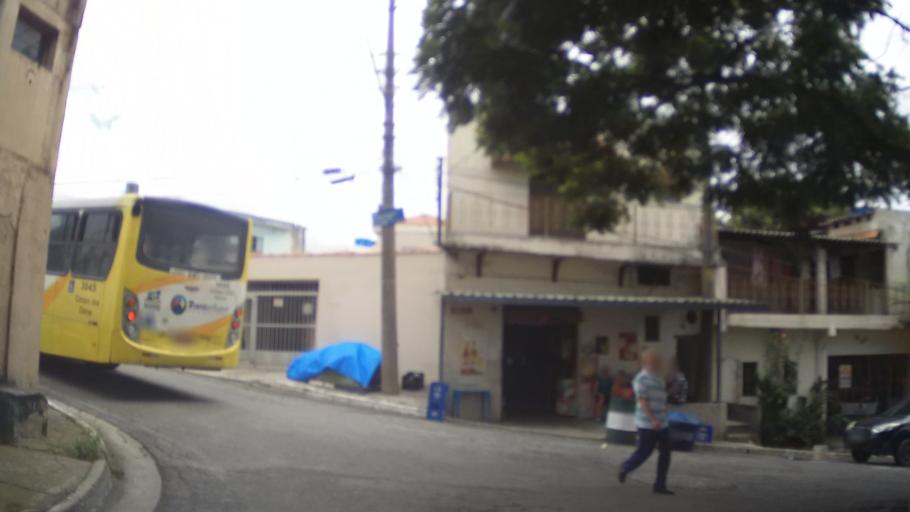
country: BR
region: Sao Paulo
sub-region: Guarulhos
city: Guarulhos
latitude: -23.4933
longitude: -46.5580
